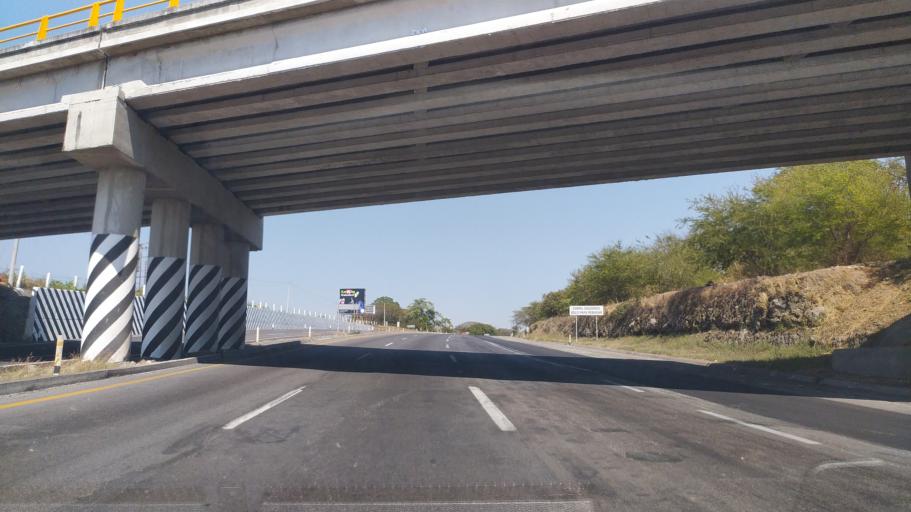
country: MX
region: Colima
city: Cuauhtemoc
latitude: 19.2923
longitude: -103.6502
